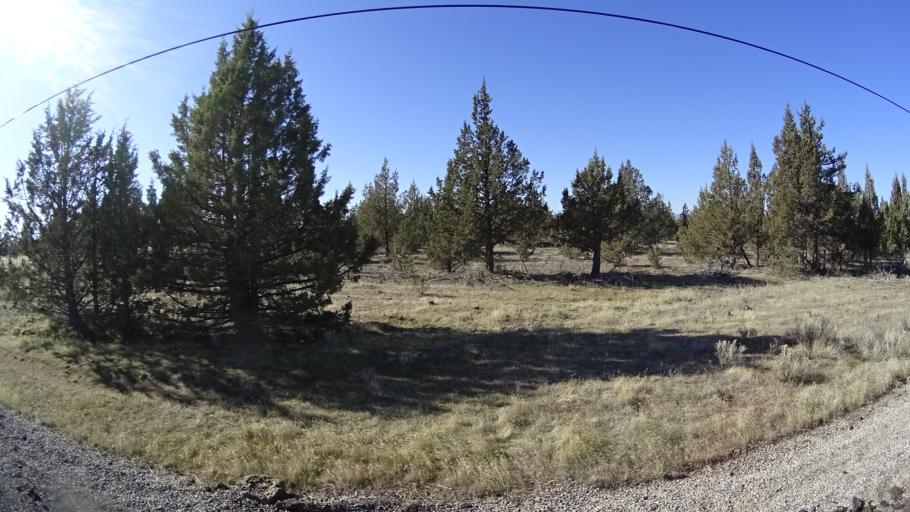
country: US
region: California
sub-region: Siskiyou County
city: Montague
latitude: 41.6526
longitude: -122.3608
